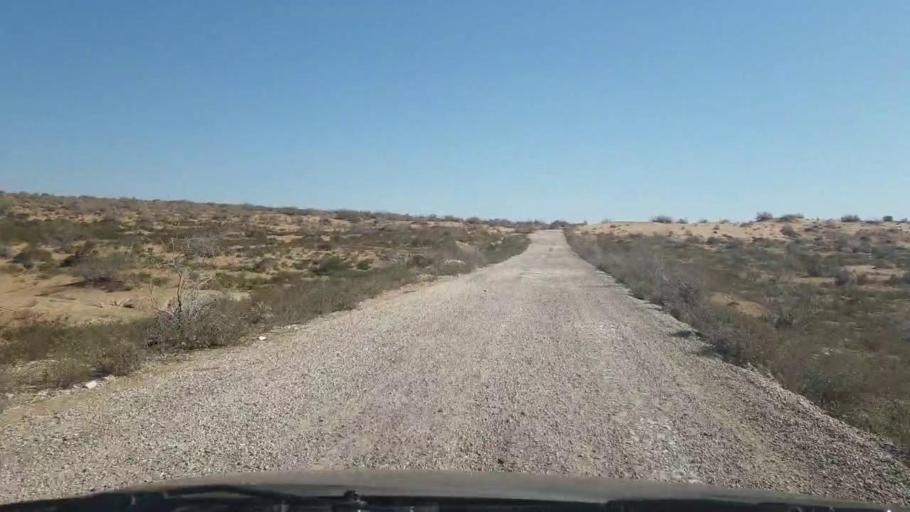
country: PK
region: Sindh
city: Bozdar
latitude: 27.0187
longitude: 68.7316
